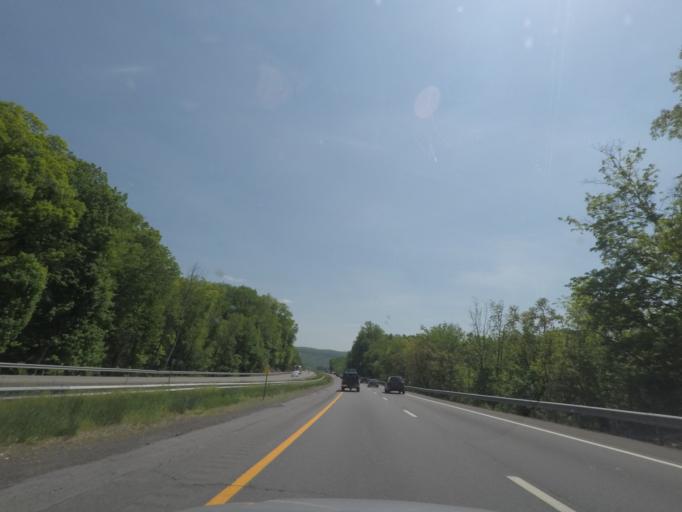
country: US
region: New York
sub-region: Orange County
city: Central Valley
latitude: 41.3388
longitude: -74.1171
